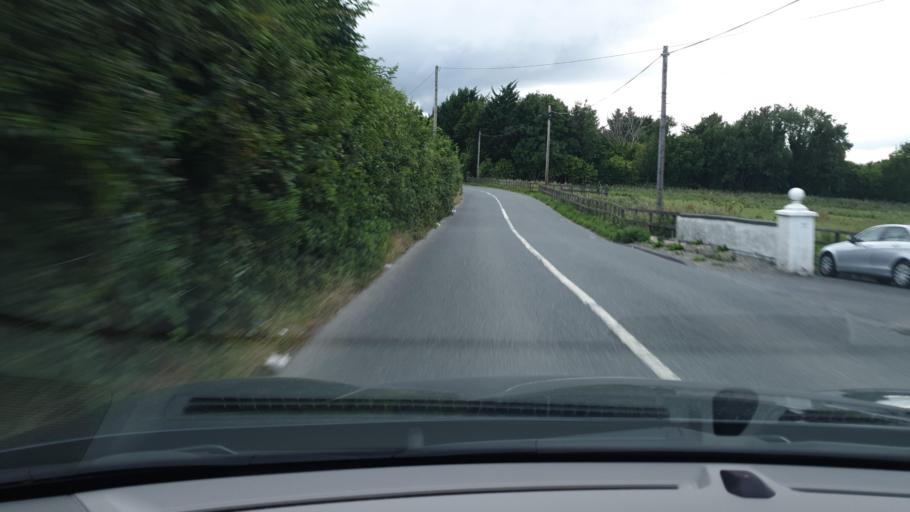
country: IE
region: Leinster
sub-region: South Dublin
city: Saggart
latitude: 53.2743
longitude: -6.4350
